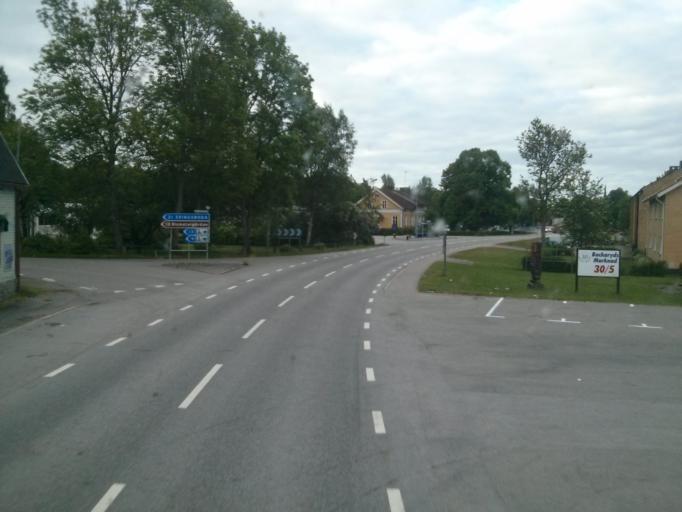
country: SE
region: Blekinge
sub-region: Ronneby Kommun
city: Brakne-Hoby
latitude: 56.3485
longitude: 15.1526
